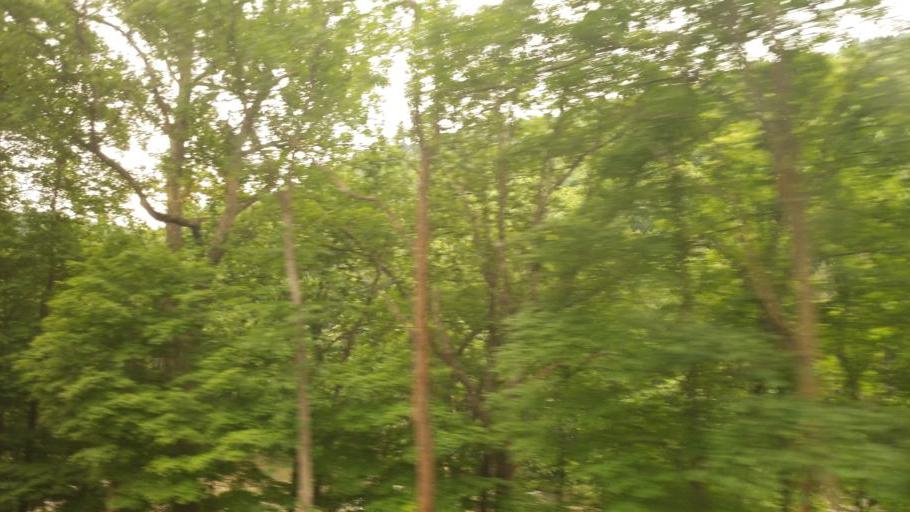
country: US
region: Pennsylvania
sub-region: Fayette County
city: South Connellsville
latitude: 39.9220
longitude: -79.4768
